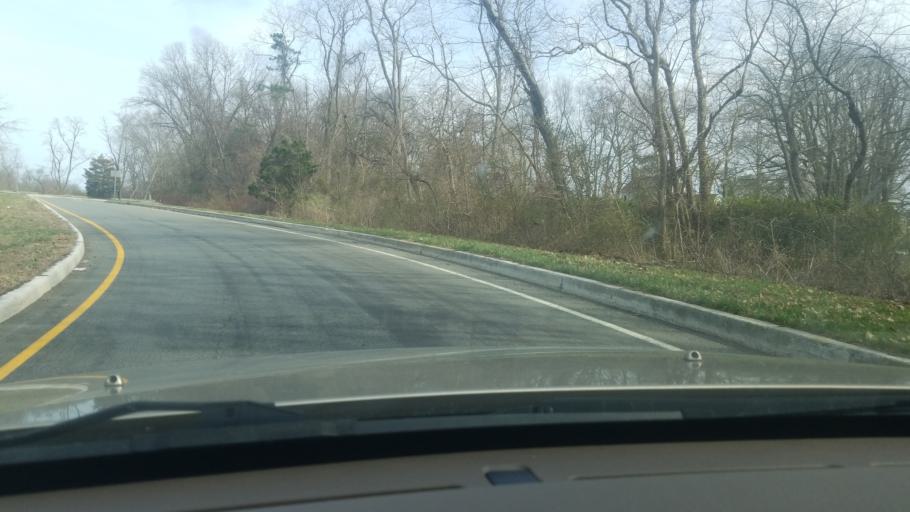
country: US
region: New Jersey
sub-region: Monmouth County
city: West Freehold
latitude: 40.2496
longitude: -74.3112
